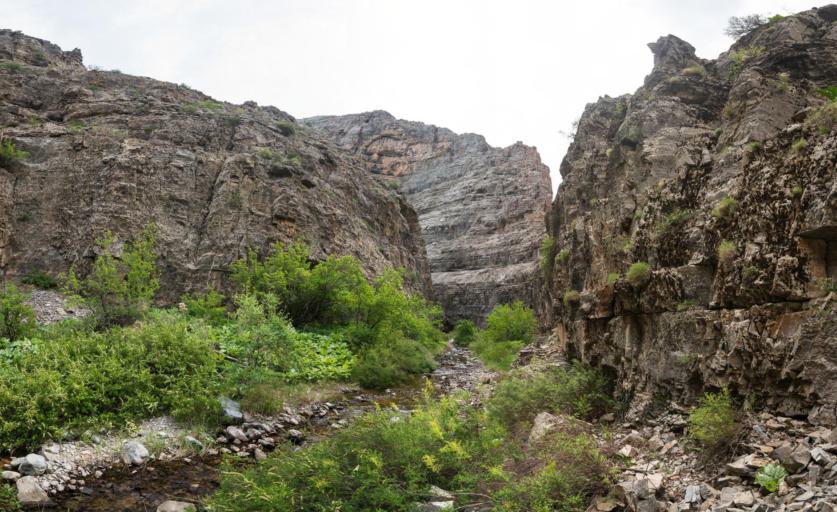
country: KZ
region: Ongtustik Qazaqstan
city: Ashchysay
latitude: 43.5285
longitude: 68.8454
